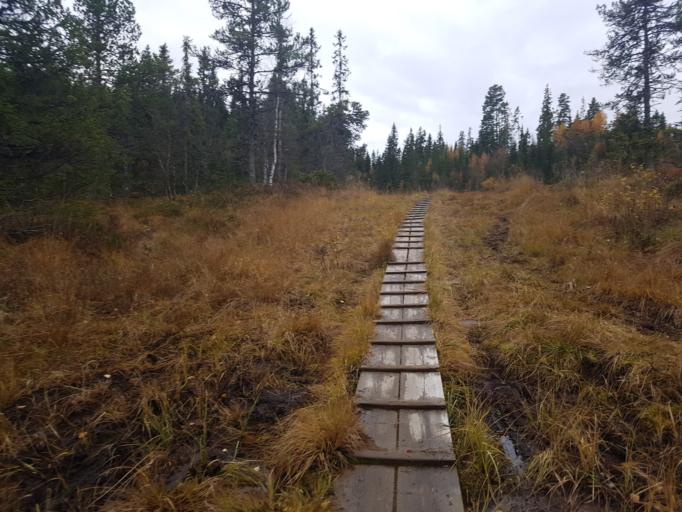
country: NO
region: Sor-Trondelag
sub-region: Melhus
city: Melhus
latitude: 63.3870
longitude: 10.2429
